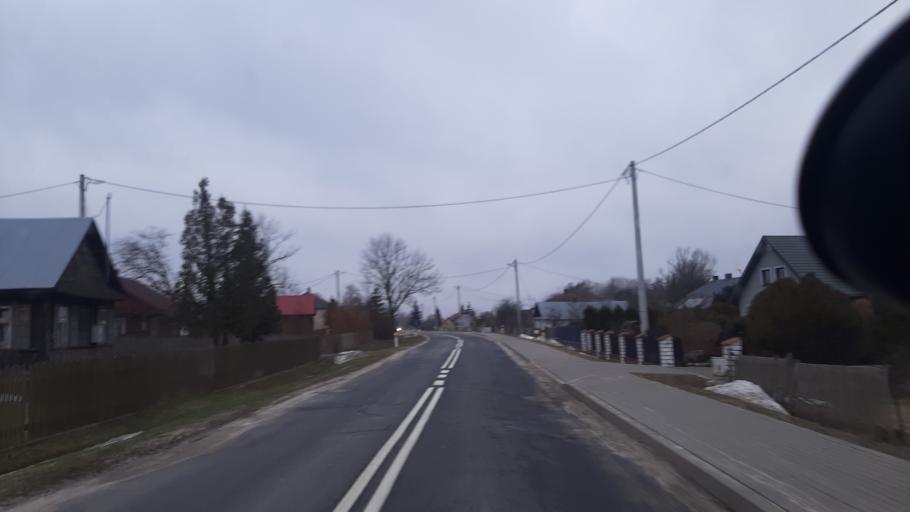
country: PL
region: Lublin Voivodeship
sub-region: Powiat wlodawski
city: Hansk
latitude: 51.5630
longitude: 23.3615
